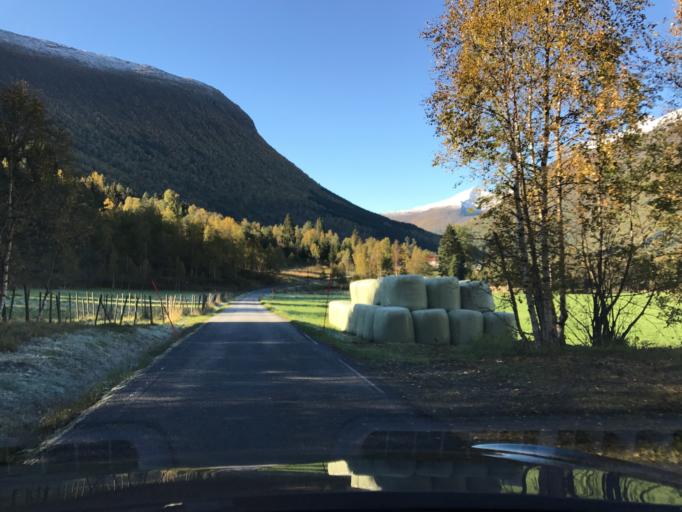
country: NO
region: More og Romsdal
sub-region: Norddal
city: Valldal
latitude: 62.3310
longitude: 7.3864
